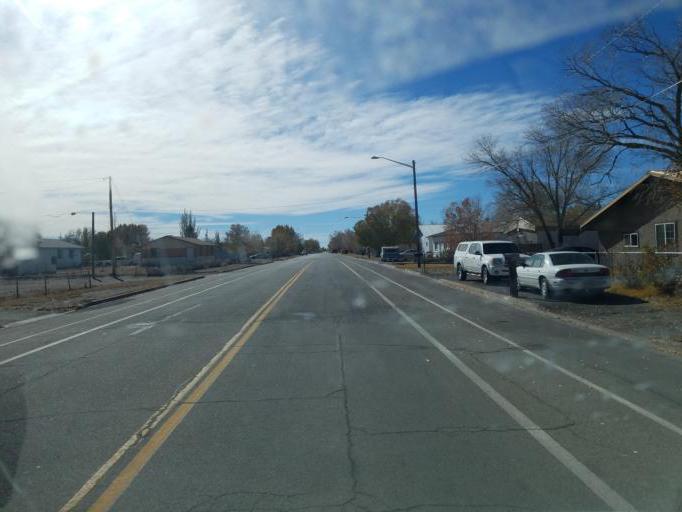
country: US
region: Colorado
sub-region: Alamosa County
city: Alamosa
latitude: 37.4611
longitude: -105.8702
